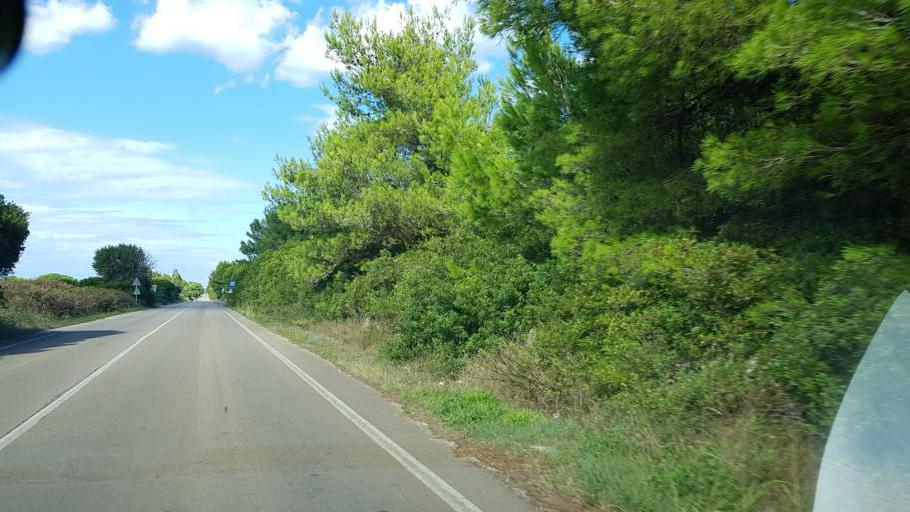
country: IT
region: Apulia
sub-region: Provincia di Lecce
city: Borgagne
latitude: 40.2416
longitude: 18.4436
